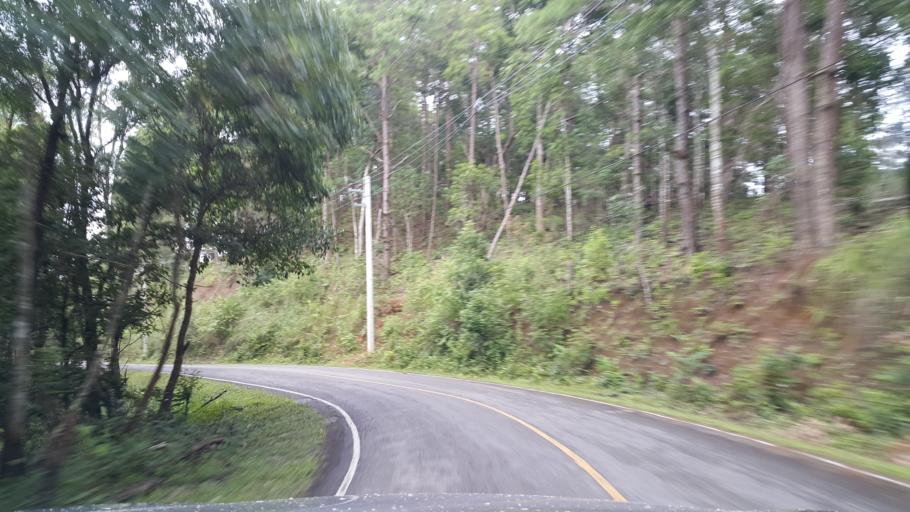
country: TH
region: Chiang Mai
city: Samoeng
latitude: 18.9065
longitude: 98.5054
